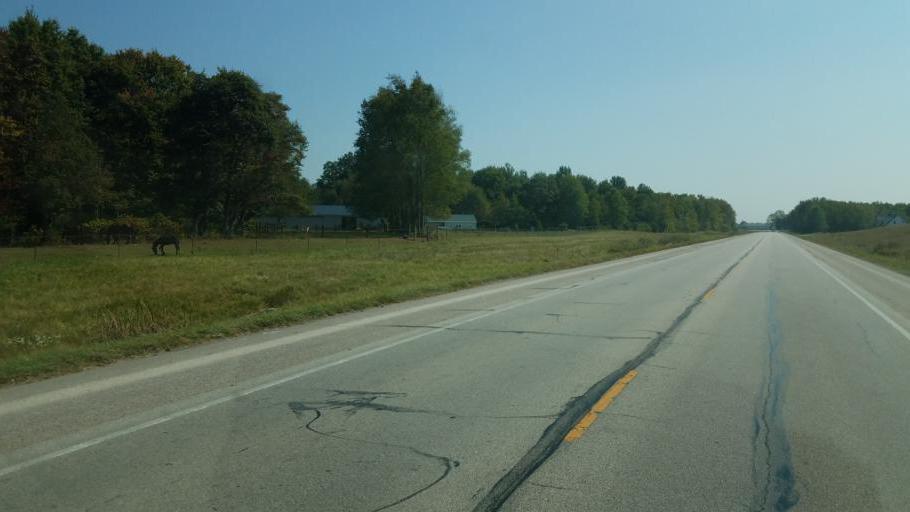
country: US
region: Indiana
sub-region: LaGrange County
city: Topeka
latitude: 41.6448
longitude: -85.5553
